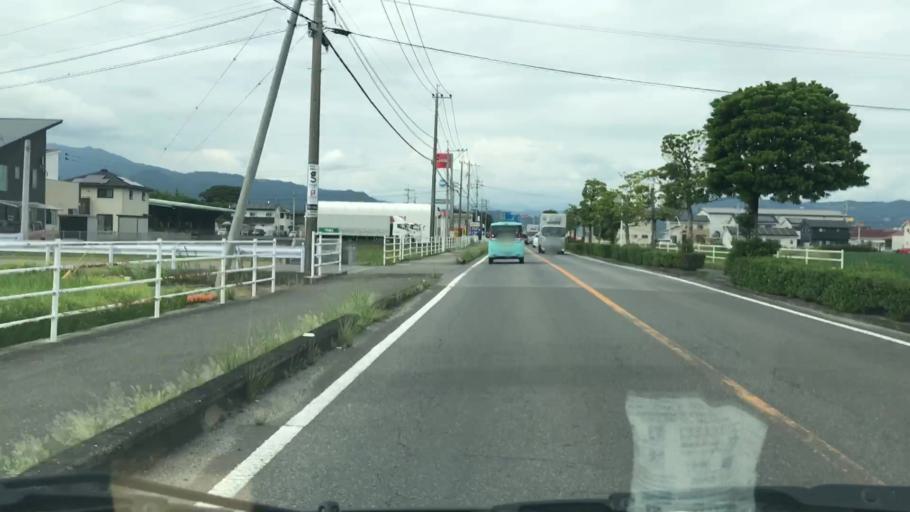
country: JP
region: Saga Prefecture
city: Saga-shi
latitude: 33.2731
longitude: 130.2609
